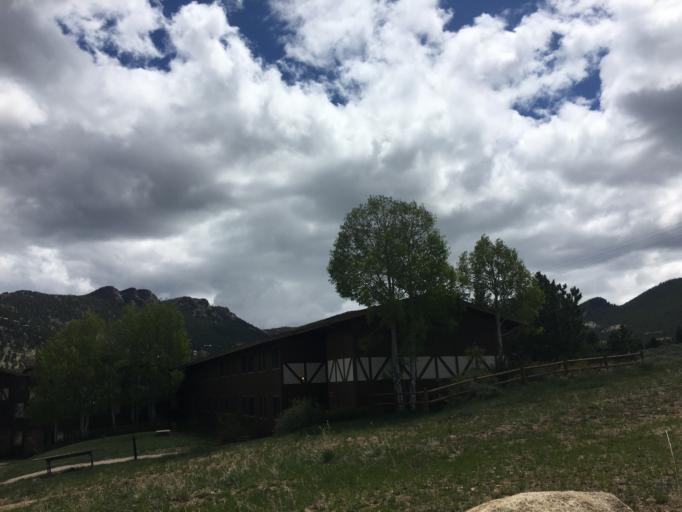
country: US
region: Colorado
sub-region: Larimer County
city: Estes Park
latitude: 40.3401
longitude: -105.5772
